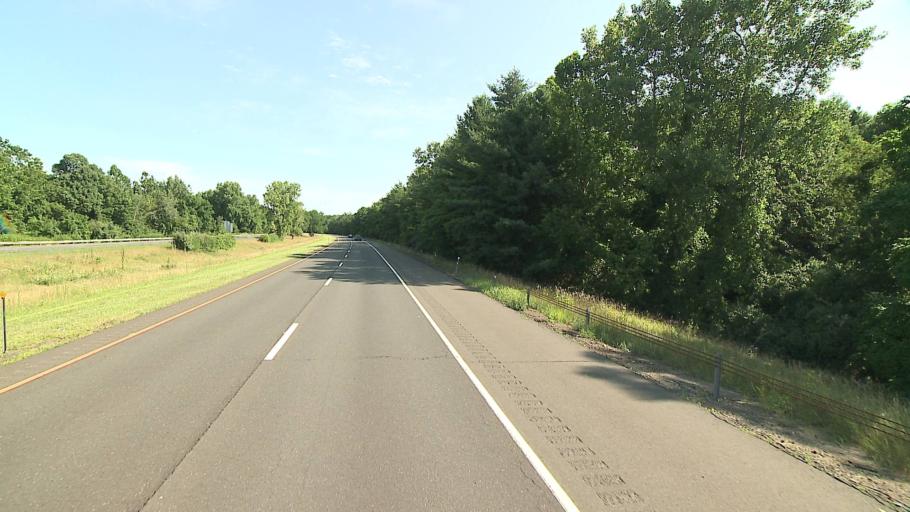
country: US
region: Connecticut
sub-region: Fairfield County
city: Bethel
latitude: 41.4459
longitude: -73.3959
